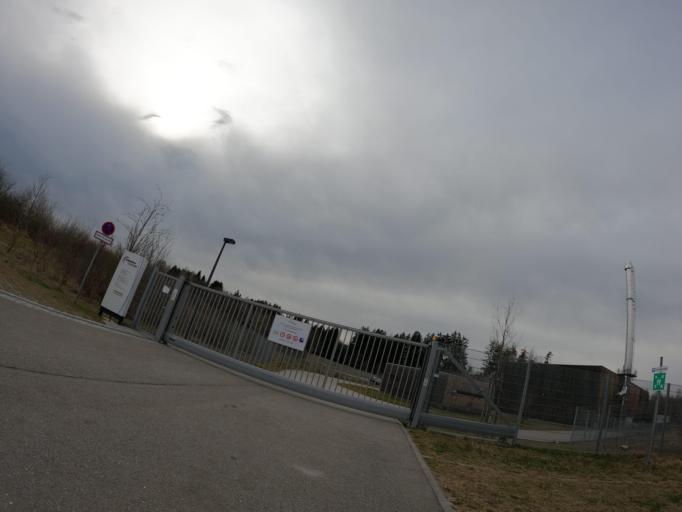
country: DE
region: Bavaria
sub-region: Upper Bavaria
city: Oberhaching
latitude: 48.0194
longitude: 11.5638
